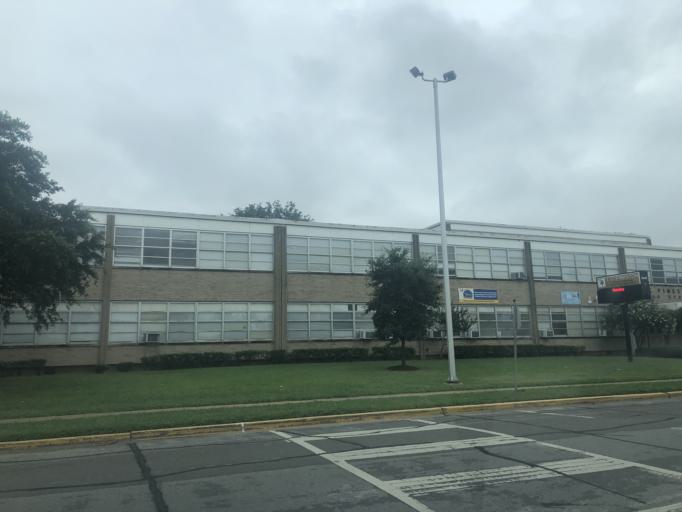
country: US
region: Texas
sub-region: Dallas County
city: Dallas
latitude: 32.7822
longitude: -96.8582
